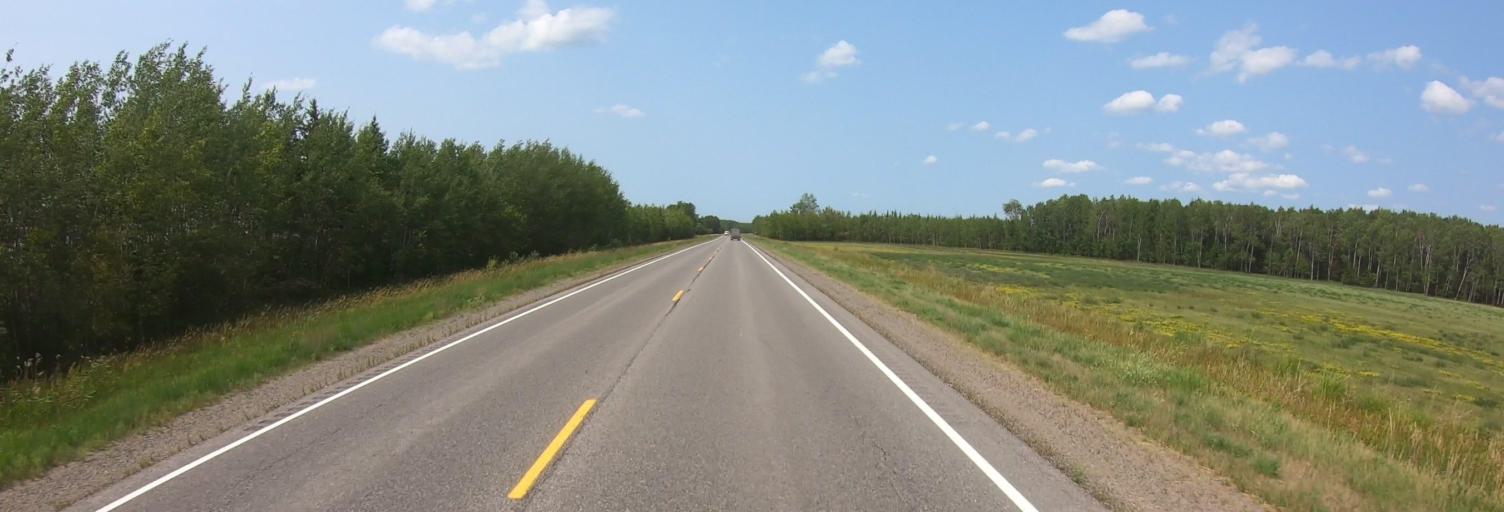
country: US
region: Minnesota
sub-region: Lake of the Woods County
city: Baudette
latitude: 48.6323
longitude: -94.1188
